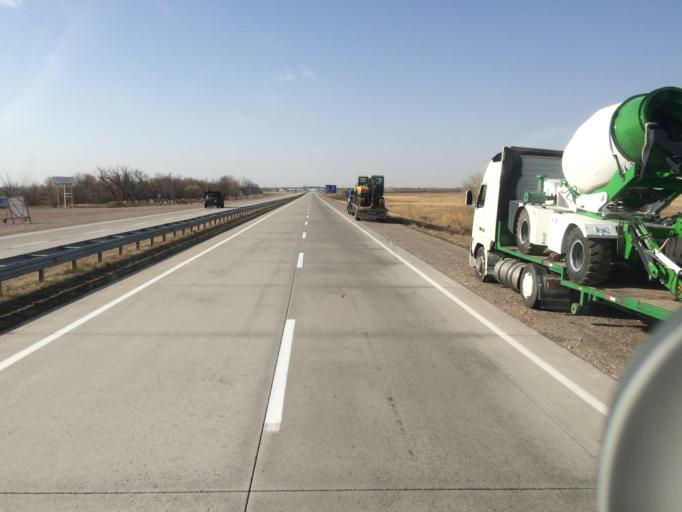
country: KZ
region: Zhambyl
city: Oytal
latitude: 42.9274
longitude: 73.2551
